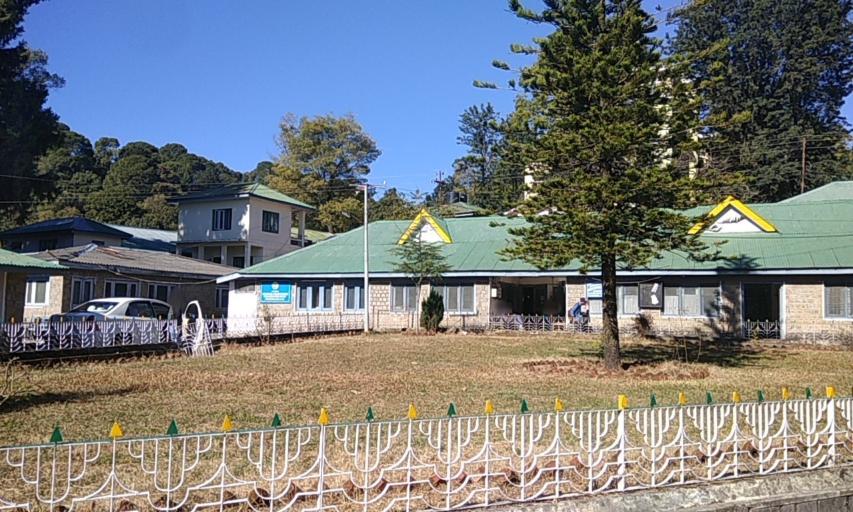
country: IN
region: Himachal Pradesh
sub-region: Kangra
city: Dharmsala
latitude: 32.2103
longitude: 76.3207
